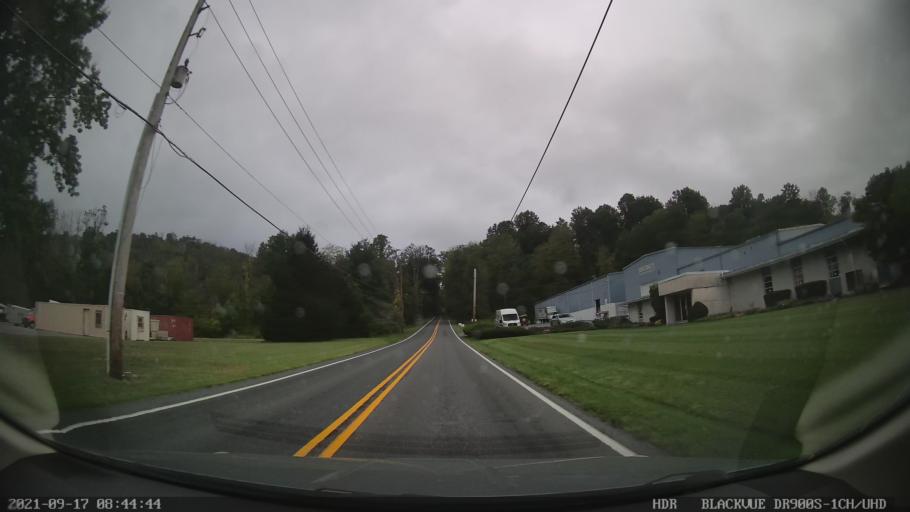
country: US
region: Pennsylvania
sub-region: Berks County
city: Oley
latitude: 40.3687
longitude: -75.8215
